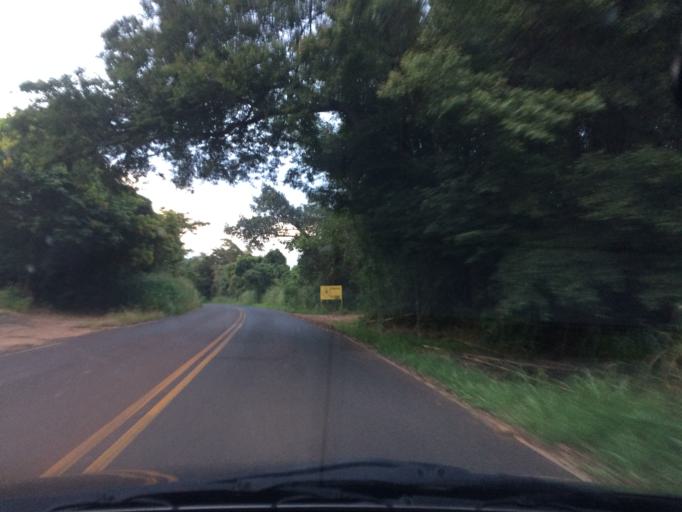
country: BR
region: Sao Paulo
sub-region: Tambau
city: Tambau
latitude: -21.7265
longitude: -47.1848
